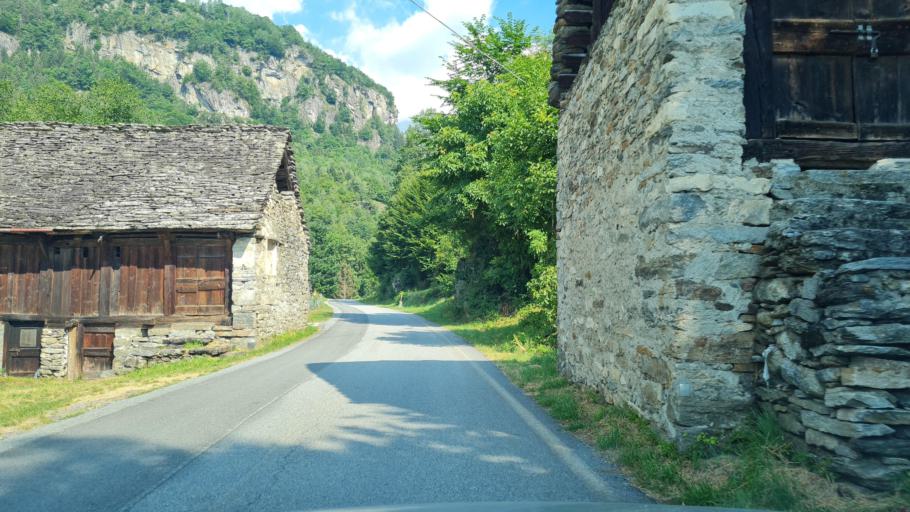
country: IT
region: Piedmont
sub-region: Provincia Verbano-Cusio-Ossola
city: Baceno
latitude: 46.2743
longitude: 8.2993
